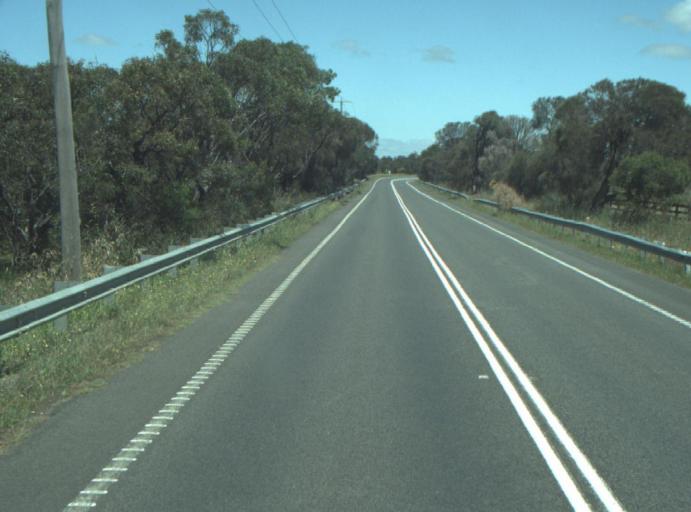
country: AU
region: Victoria
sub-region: Queenscliffe
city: Queenscliff
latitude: -38.1847
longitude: 144.6838
